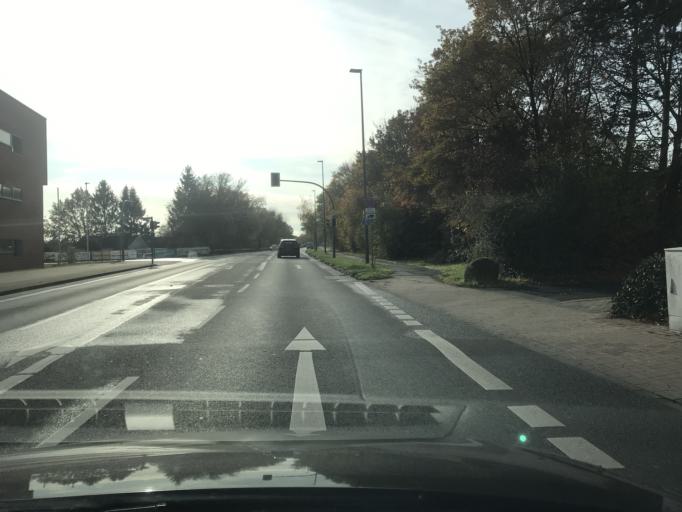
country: DE
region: North Rhine-Westphalia
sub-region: Regierungsbezirk Arnsberg
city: Hamm
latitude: 51.6772
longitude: 7.8513
